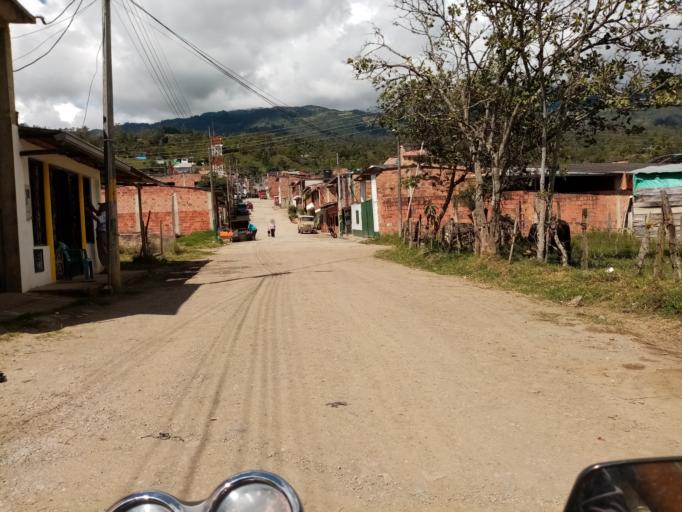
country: CO
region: Cundinamarca
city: Tenza
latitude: 5.0967
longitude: -73.4434
